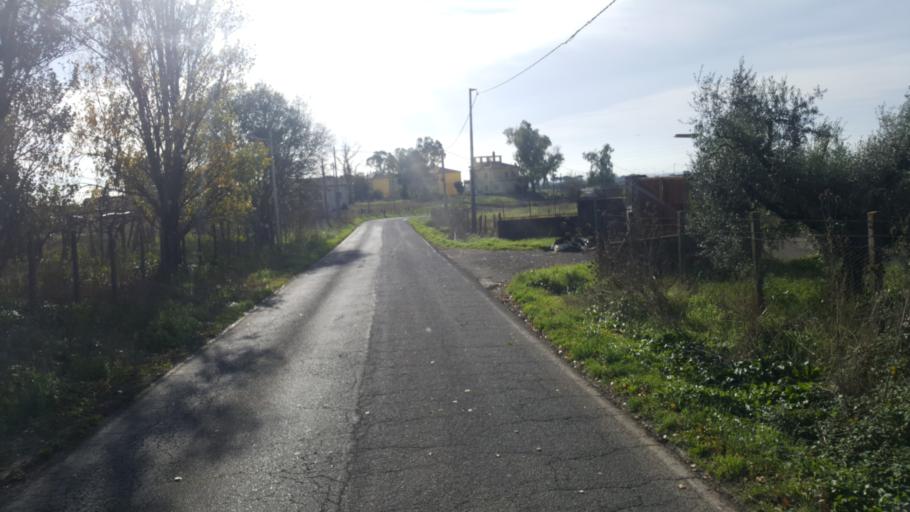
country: IT
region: Latium
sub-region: Citta metropolitana di Roma Capitale
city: Mantiglia di Ardea
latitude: 41.6616
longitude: 12.6303
